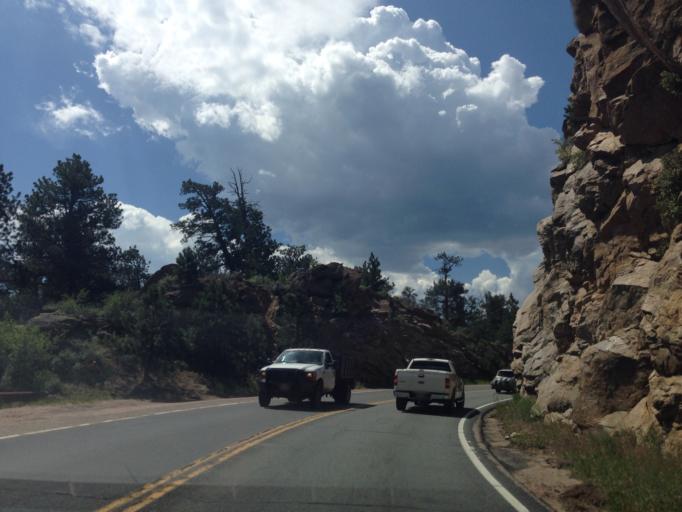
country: US
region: Colorado
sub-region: Larimer County
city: Estes Park
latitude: 40.3783
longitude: -105.4787
